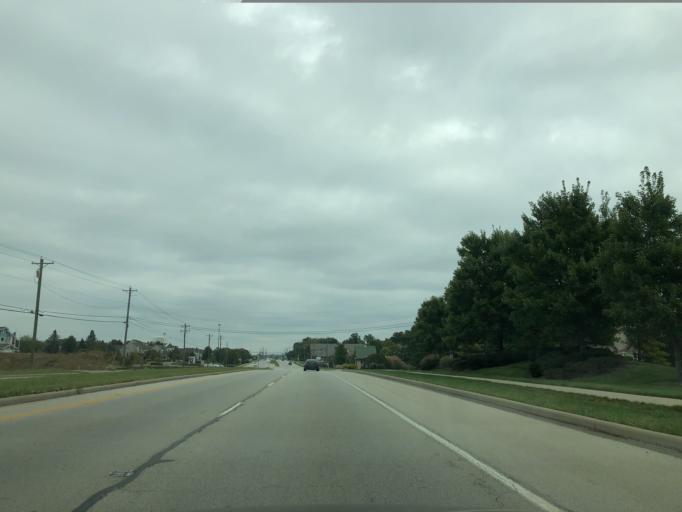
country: US
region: Ohio
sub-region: Warren County
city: Landen
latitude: 39.2982
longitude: -84.2890
